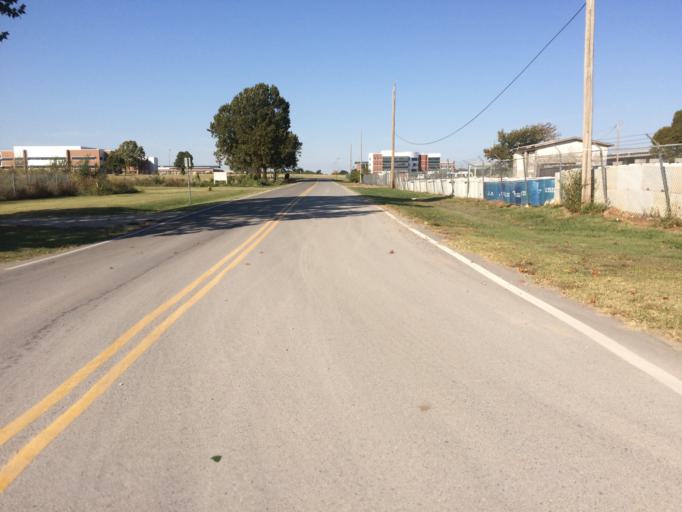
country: US
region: Oklahoma
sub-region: Cleveland County
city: Norman
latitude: 35.1851
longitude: -97.4332
